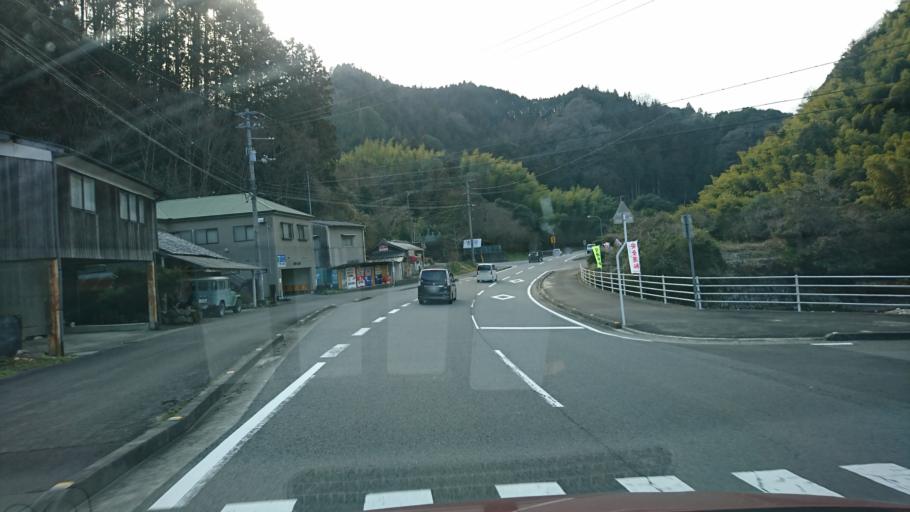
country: JP
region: Ehime
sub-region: Shikoku-chuo Shi
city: Matsuyama
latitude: 33.8971
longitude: 132.8603
